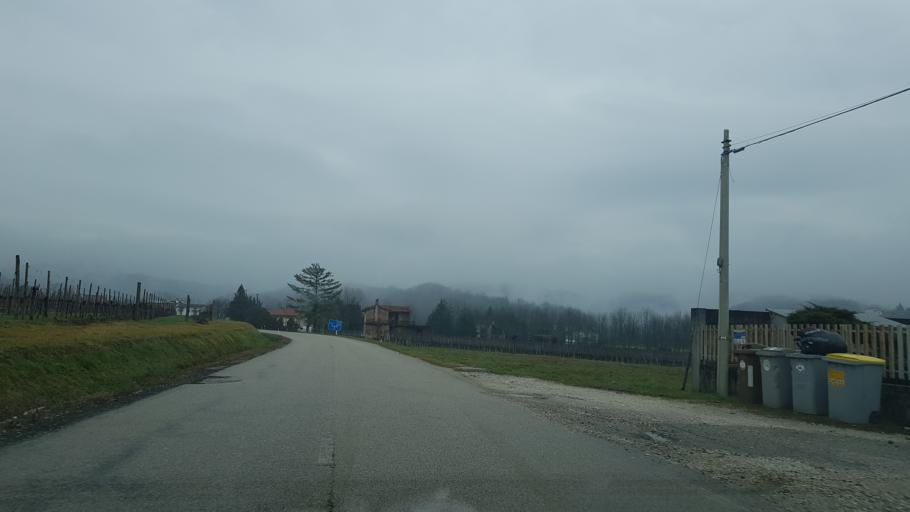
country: IT
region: Friuli Venezia Giulia
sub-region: Provincia di Udine
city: Prepotto
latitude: 46.0554
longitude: 13.4553
